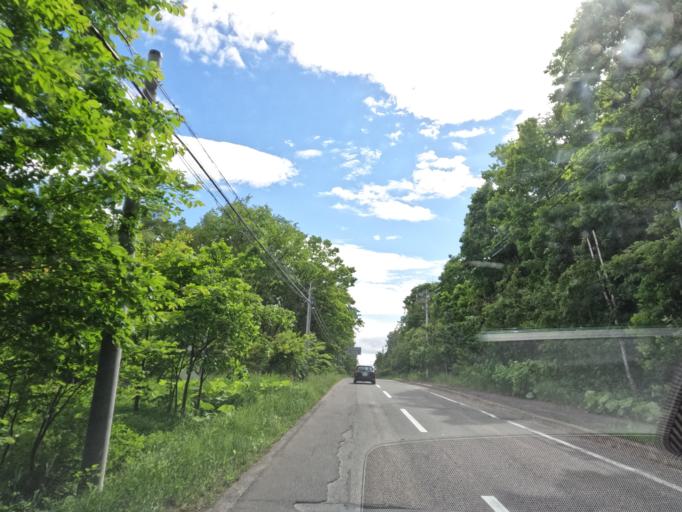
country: JP
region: Hokkaido
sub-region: Asahikawa-shi
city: Asahikawa
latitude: 43.8345
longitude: 142.5358
